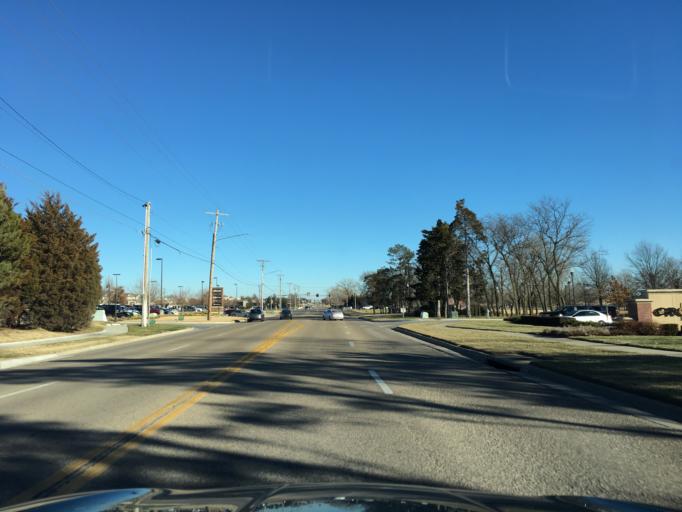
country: US
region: Kansas
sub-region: Sedgwick County
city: Bellaire
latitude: 37.7084
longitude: -97.2292
